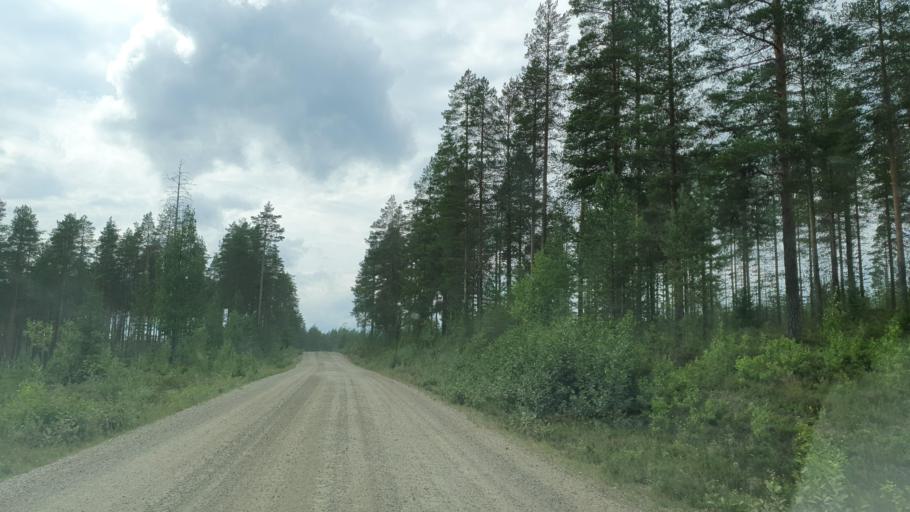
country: FI
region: Kainuu
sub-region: Kehys-Kainuu
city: Kuhmo
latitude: 64.7251
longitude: 29.7002
